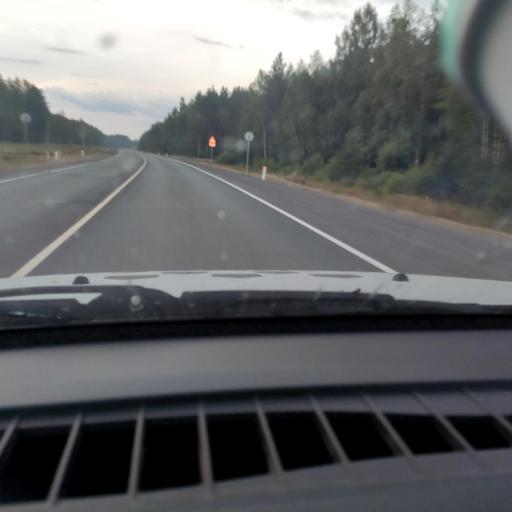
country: RU
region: Kirov
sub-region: Kirovo-Chepetskiy Rayon
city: Kirov
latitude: 58.6909
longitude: 49.6241
